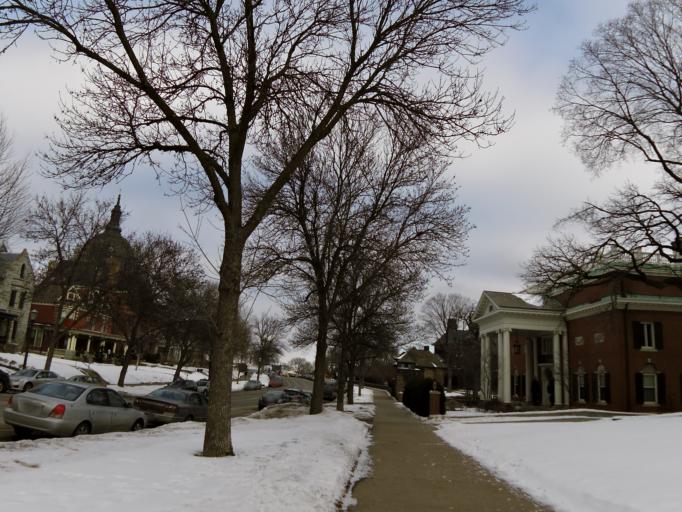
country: US
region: Minnesota
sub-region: Ramsey County
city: Saint Paul
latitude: 44.9447
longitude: -93.1106
